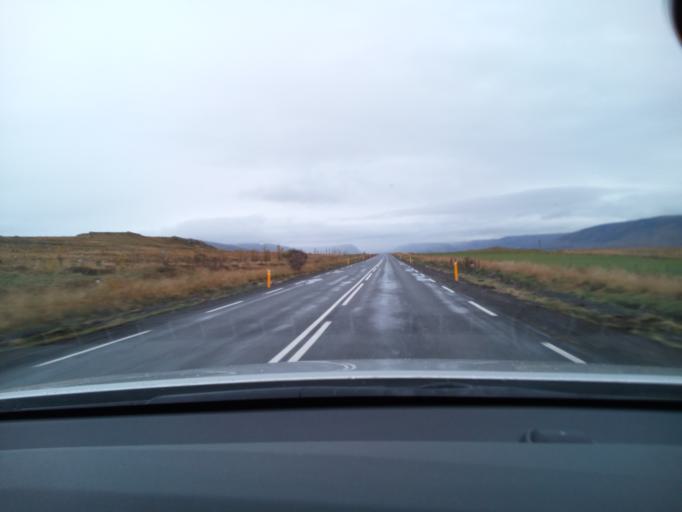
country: IS
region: Capital Region
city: Mosfellsbaer
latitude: 64.3931
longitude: -21.7192
